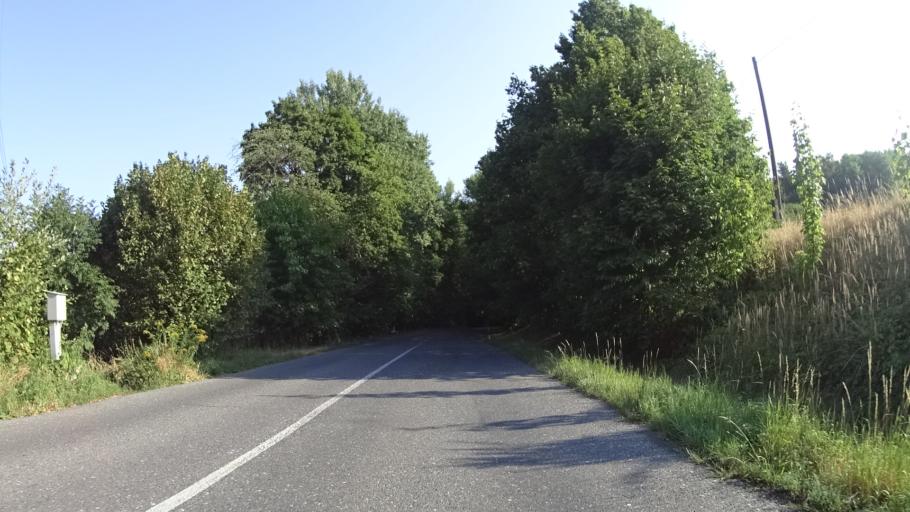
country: CZ
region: Liberecky
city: Hodkovice nad Mohelkou
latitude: 50.6496
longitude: 15.1060
